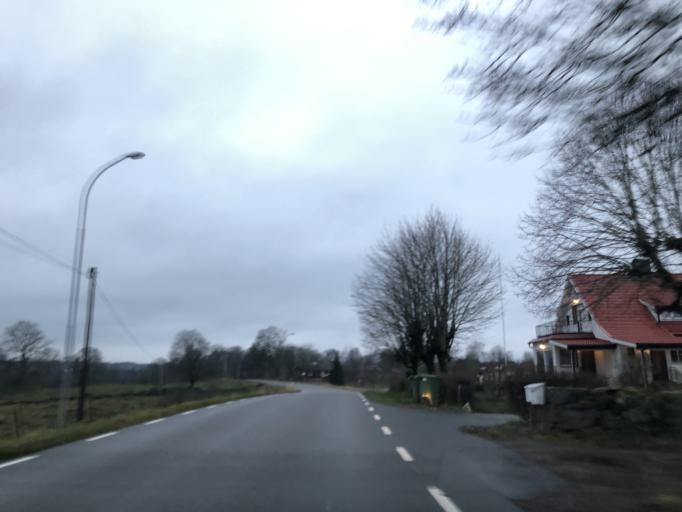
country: SE
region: Vaestra Goetaland
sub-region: Boras Kommun
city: Dalsjofors
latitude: 57.8384
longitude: 13.2238
